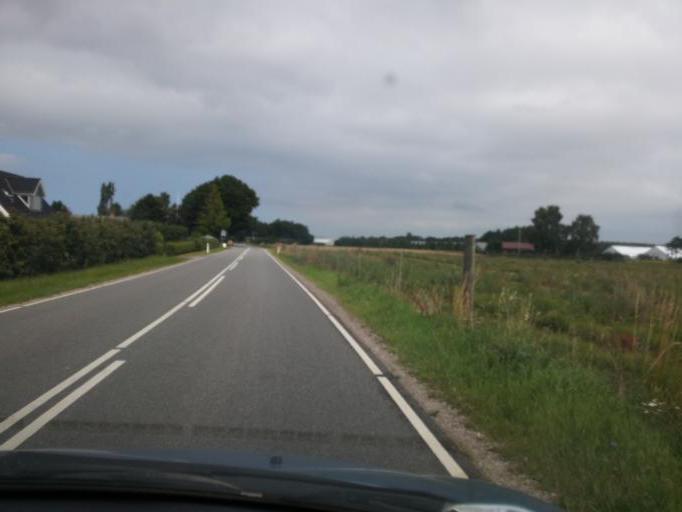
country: DK
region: South Denmark
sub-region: Kerteminde Kommune
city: Langeskov
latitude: 55.3955
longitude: 10.5528
